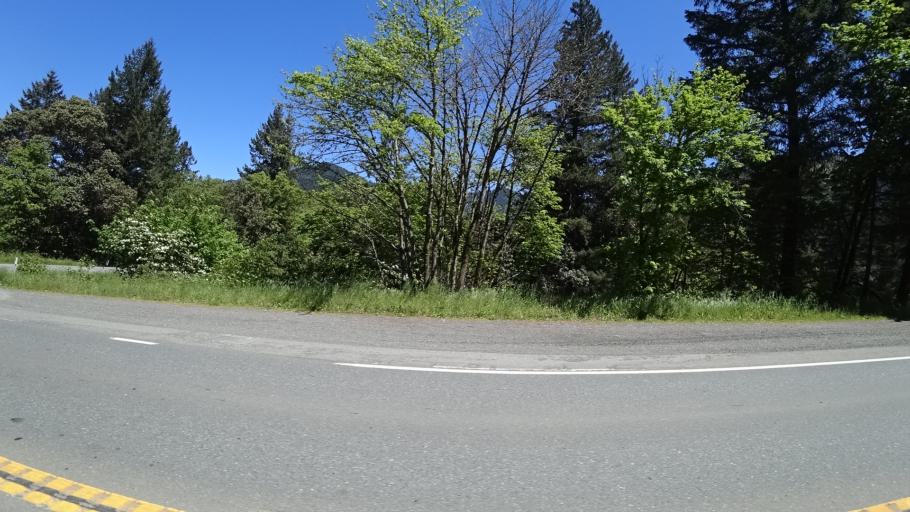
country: US
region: California
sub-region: Humboldt County
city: Willow Creek
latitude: 40.9376
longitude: -123.6267
